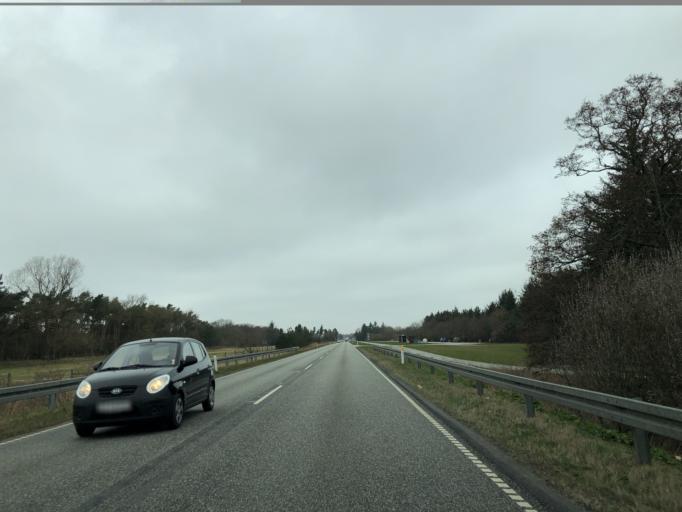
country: DK
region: North Denmark
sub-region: Frederikshavn Kommune
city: Strandby
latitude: 57.4712
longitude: 10.5014
